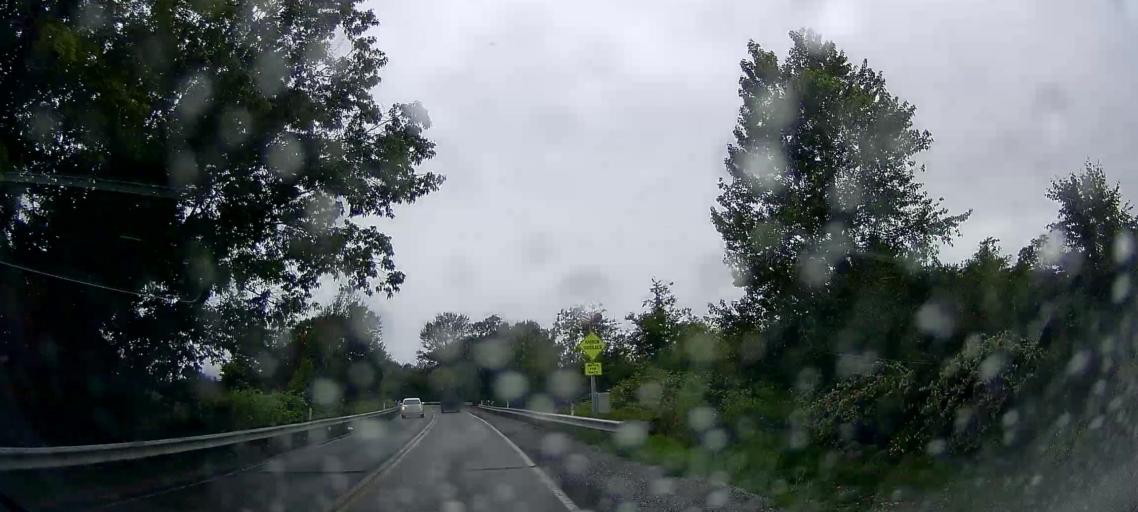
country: US
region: Washington
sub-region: Whatcom County
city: Marietta-Alderwood
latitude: 48.7827
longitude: -122.5459
